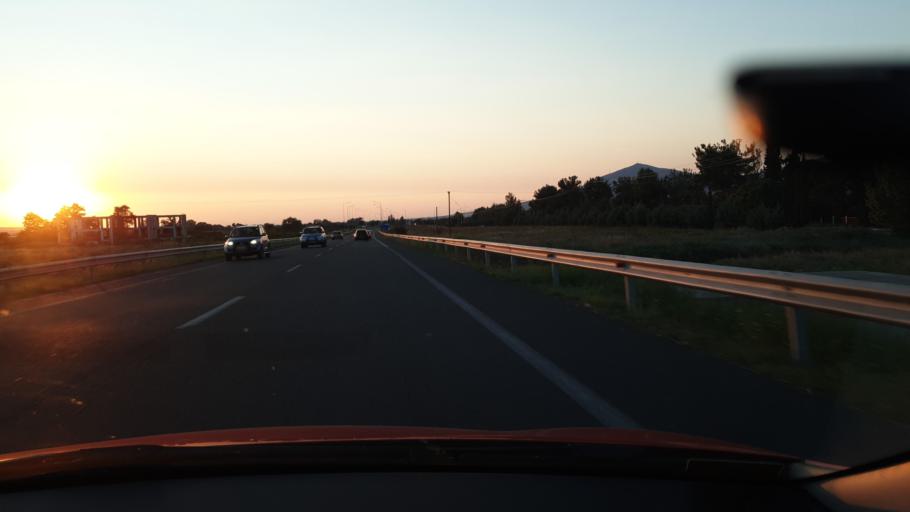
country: GR
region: Central Macedonia
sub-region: Nomos Thessalonikis
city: Vasilika
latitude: 40.4750
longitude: 23.1674
